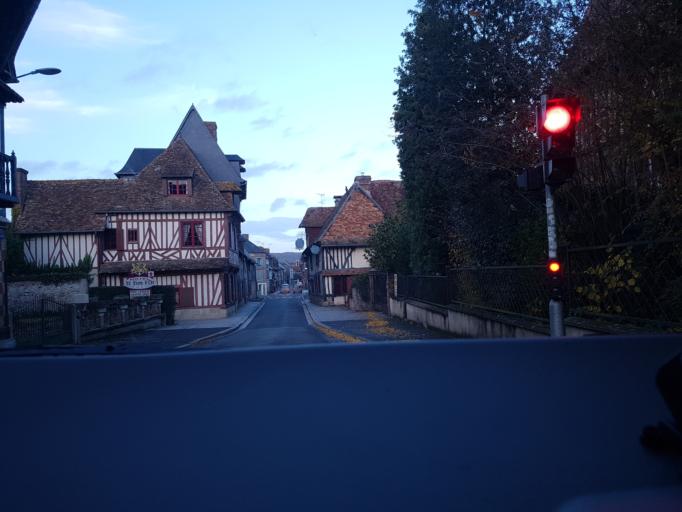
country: FR
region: Lower Normandy
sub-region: Departement du Calvados
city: Saint-Gatien-des-Bois
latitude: 49.2825
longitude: 0.1799
